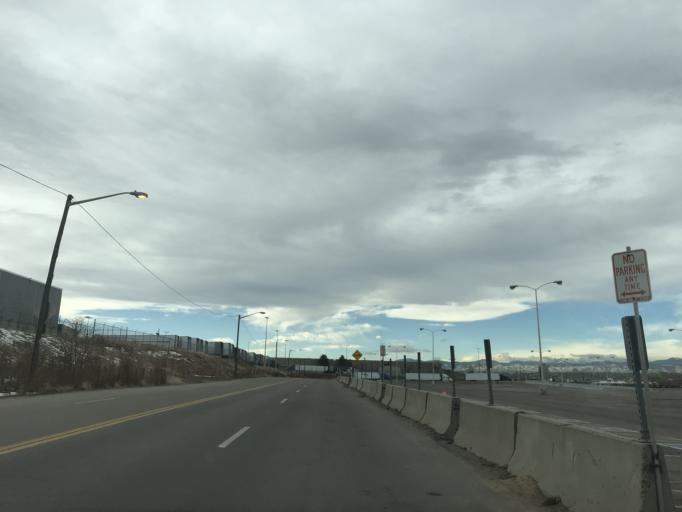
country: US
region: Colorado
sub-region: Denver County
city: Denver
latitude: 39.7782
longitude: -104.9723
